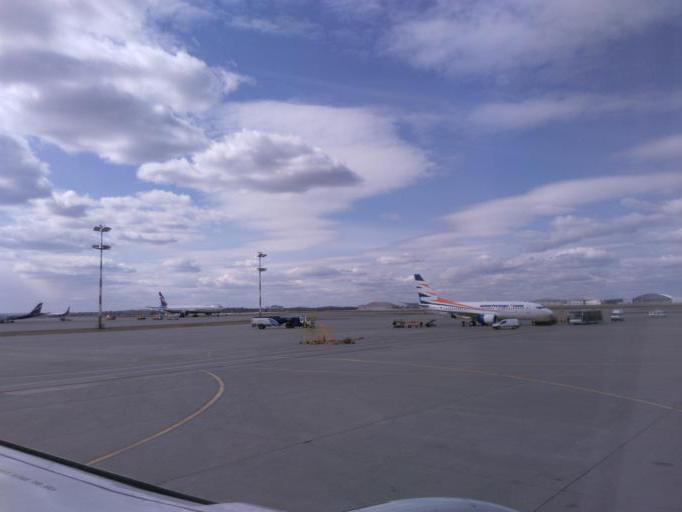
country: RU
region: Moscow
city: Khimki
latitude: 55.9656
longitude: 37.4113
